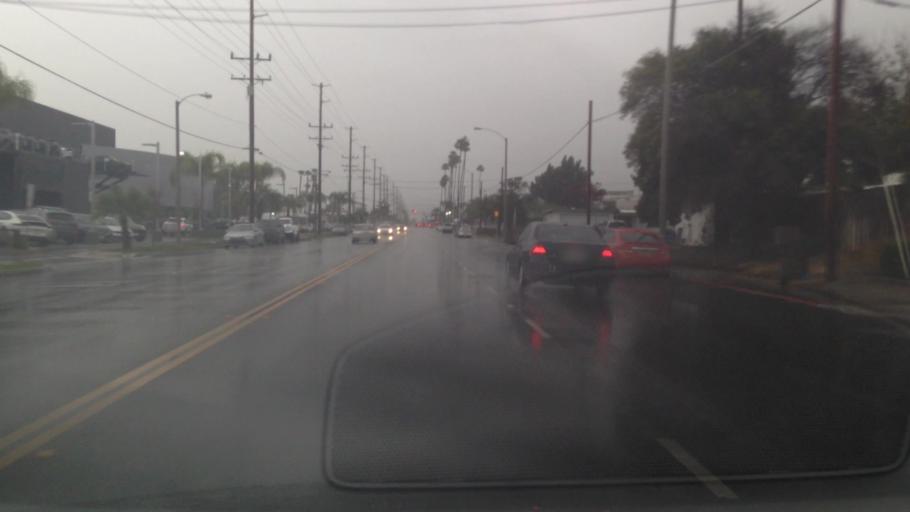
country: US
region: California
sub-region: Riverside County
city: Riverside
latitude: 33.9245
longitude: -117.4231
